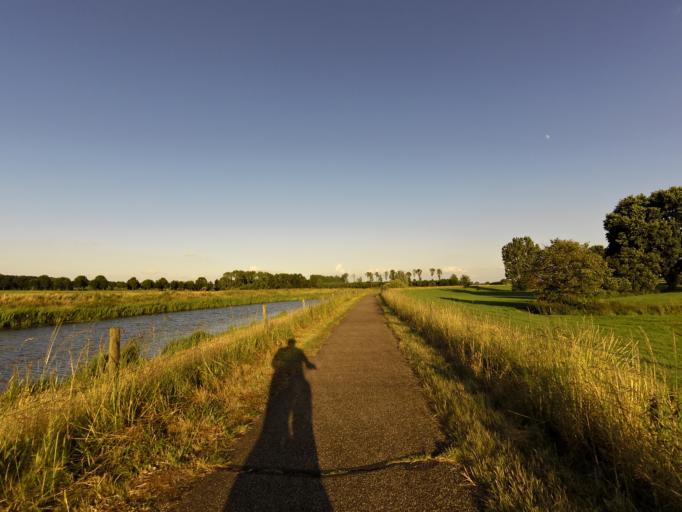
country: DE
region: North Rhine-Westphalia
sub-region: Regierungsbezirk Munster
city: Isselburg
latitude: 51.8675
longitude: 6.4486
